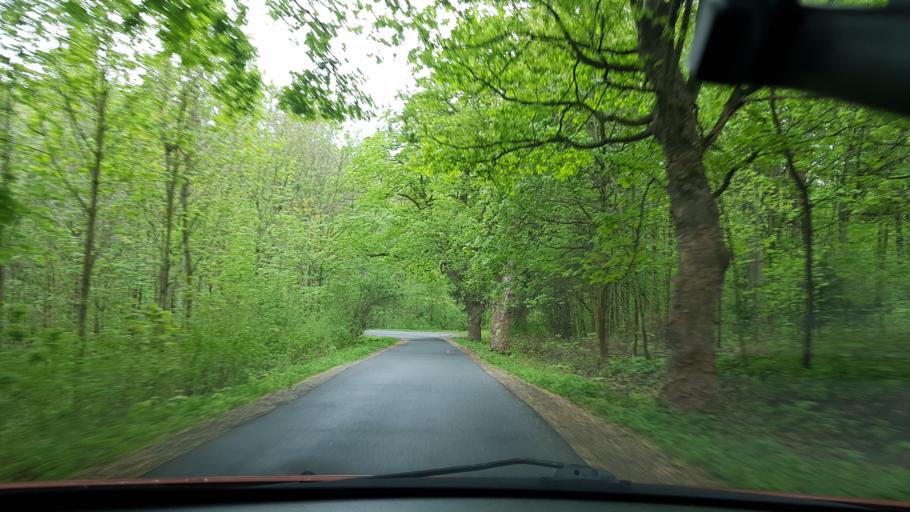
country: PL
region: Lower Silesian Voivodeship
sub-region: Powiat zabkowicki
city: Zloty Stok
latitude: 50.4457
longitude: 16.8946
